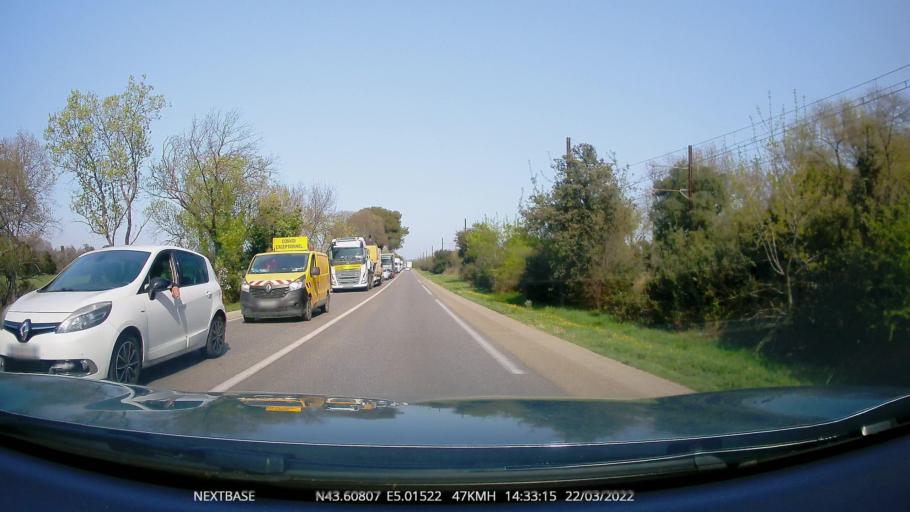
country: FR
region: Provence-Alpes-Cote d'Azur
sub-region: Departement des Bouches-du-Rhone
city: Miramas
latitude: 43.6081
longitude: 5.0153
